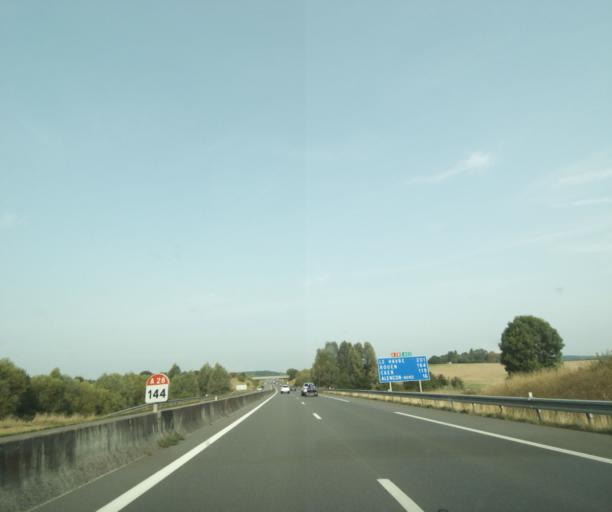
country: FR
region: Pays de la Loire
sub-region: Departement de la Sarthe
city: Champfleur
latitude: 48.3208
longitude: 0.1273
